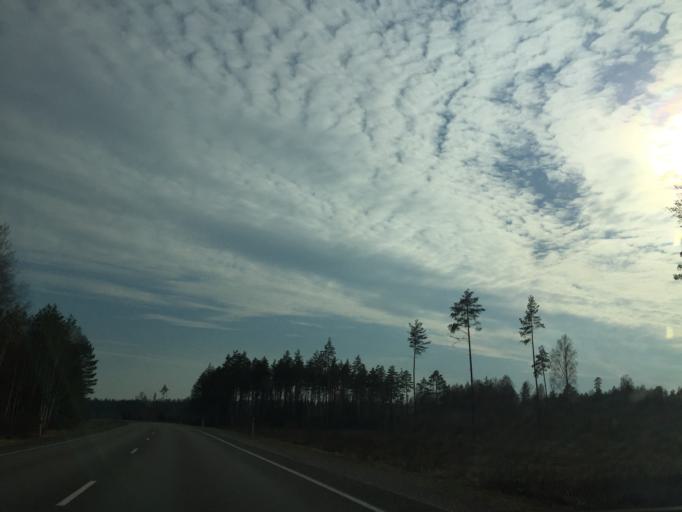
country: EE
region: Ida-Virumaa
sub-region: Kohtla-Nomme vald
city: Kohtla-Nomme
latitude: 59.0243
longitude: 27.2280
